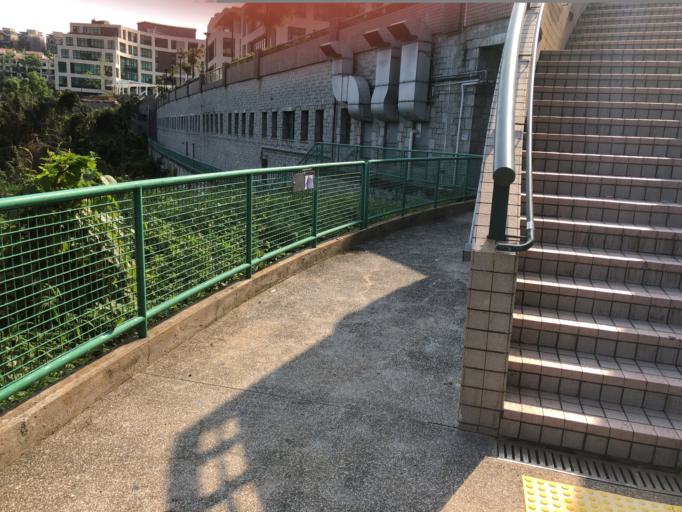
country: HK
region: Tai Po
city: Tai Po
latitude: 22.4687
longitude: 114.1947
